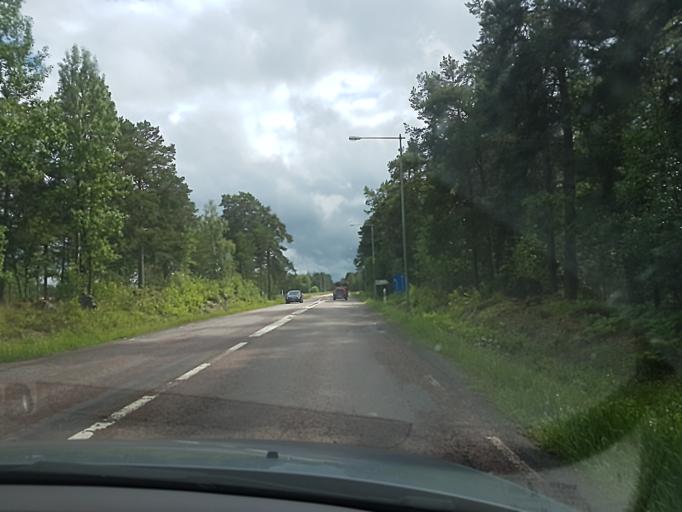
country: SE
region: Uppsala
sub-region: Osthammars Kommun
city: OEsthammar
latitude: 60.2509
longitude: 18.3476
